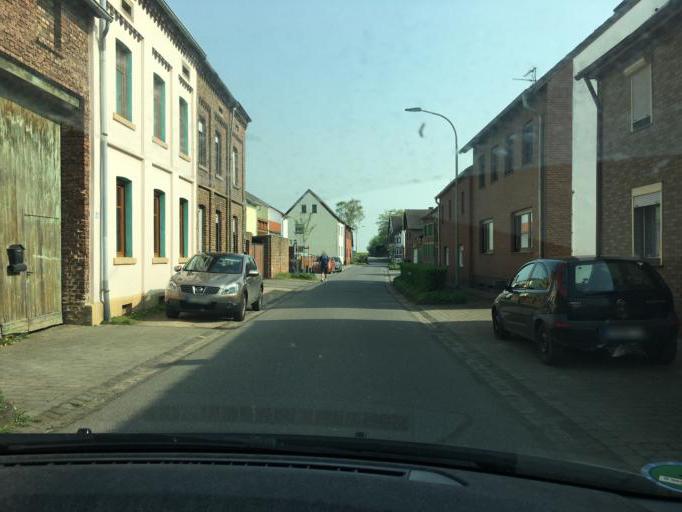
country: DE
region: North Rhine-Westphalia
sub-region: Regierungsbezirk Koln
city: Vettweiss
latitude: 50.7621
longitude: 6.5604
